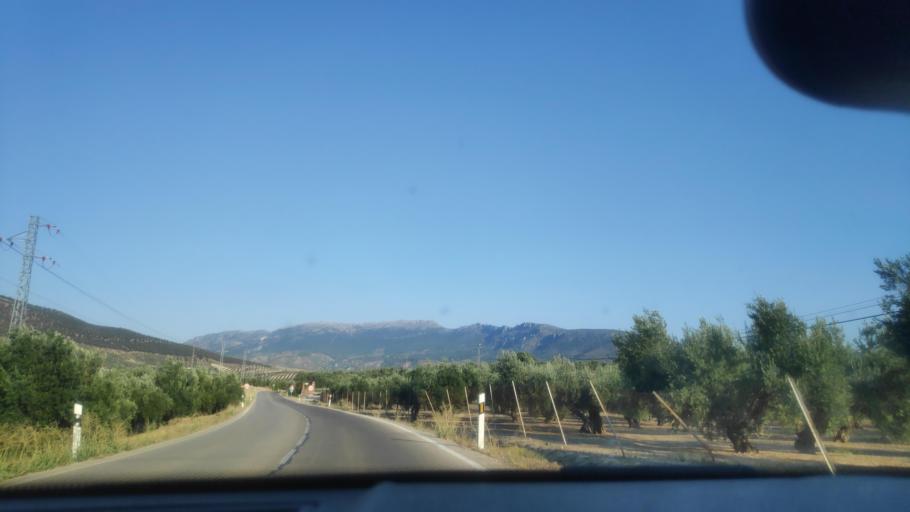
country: ES
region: Andalusia
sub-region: Provincia de Jaen
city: Jaen
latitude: 37.7312
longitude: -3.7658
